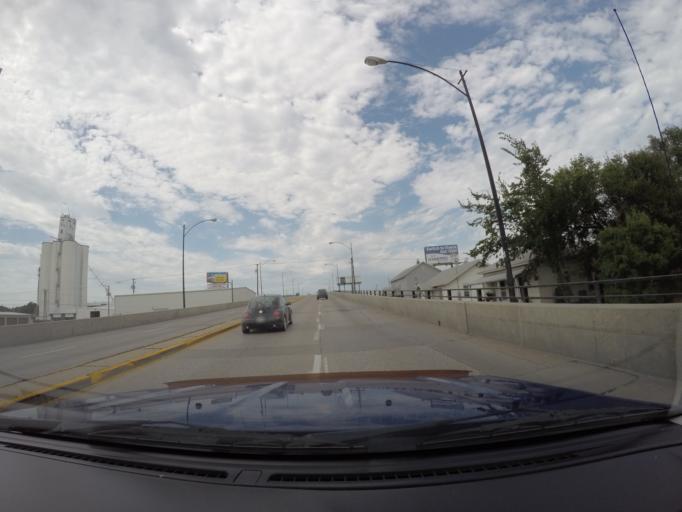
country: US
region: Nebraska
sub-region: Buffalo County
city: Kearney
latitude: 40.6929
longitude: -99.0845
